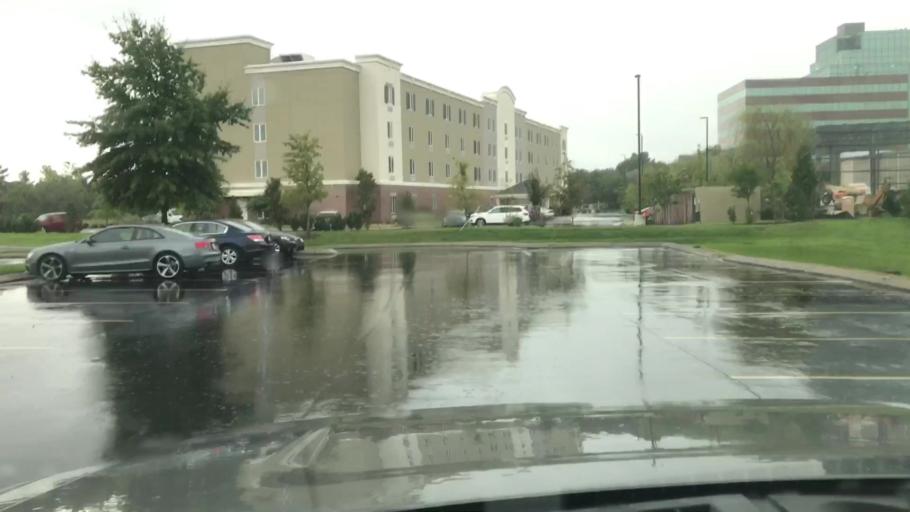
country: US
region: Tennessee
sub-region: Davidson County
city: Nashville
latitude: 36.1974
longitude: -86.7971
